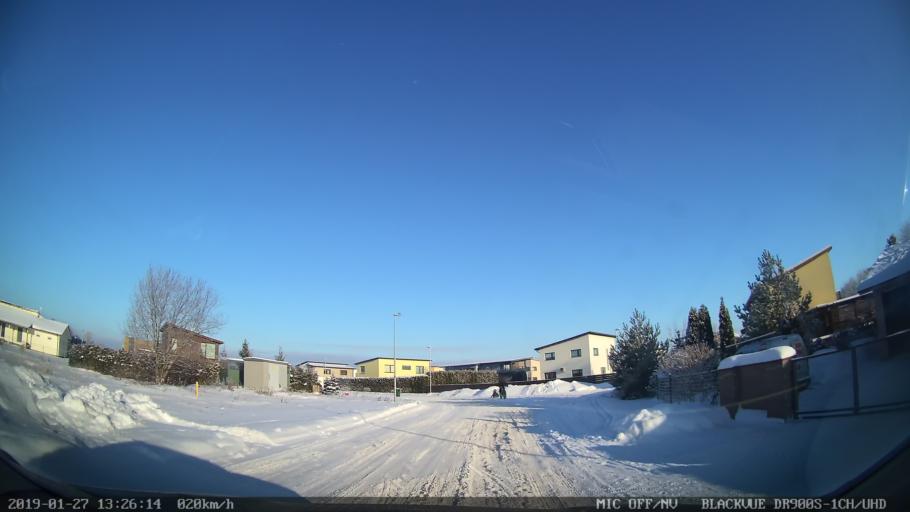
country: EE
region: Harju
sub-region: Tallinna linn
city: Tallinn
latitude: 59.3969
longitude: 24.7995
